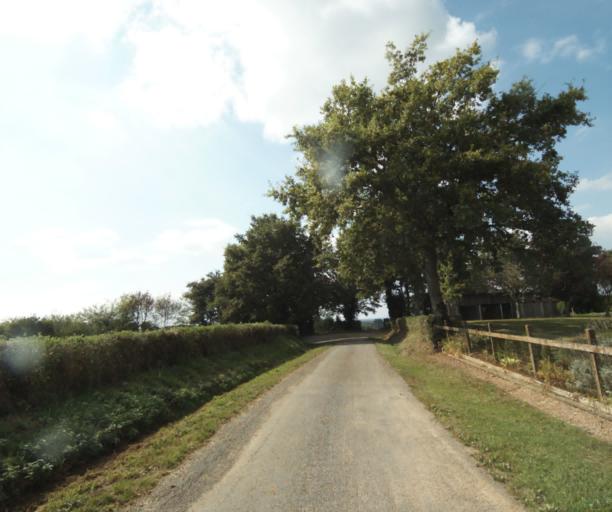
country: FR
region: Bourgogne
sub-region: Departement de Saone-et-Loire
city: Charolles
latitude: 46.4713
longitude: 4.2403
